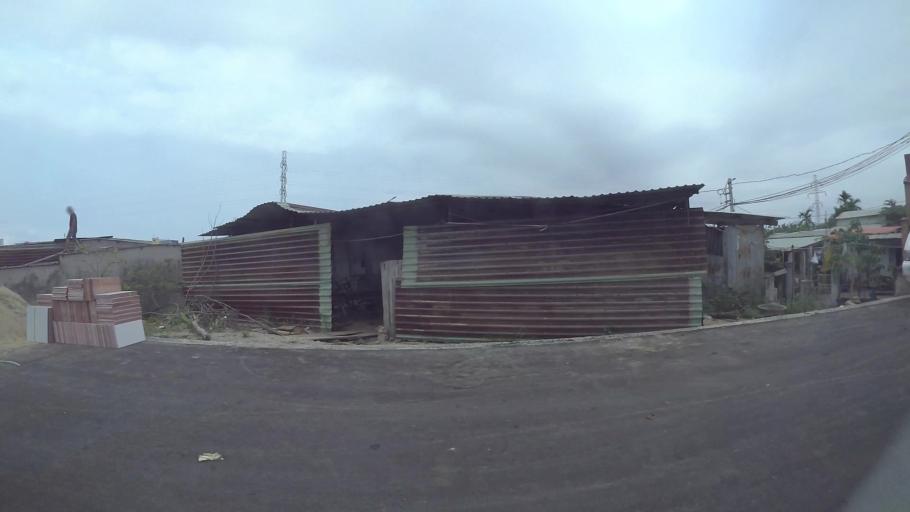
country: VN
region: Da Nang
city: Lien Chieu
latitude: 16.0486
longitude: 108.1668
